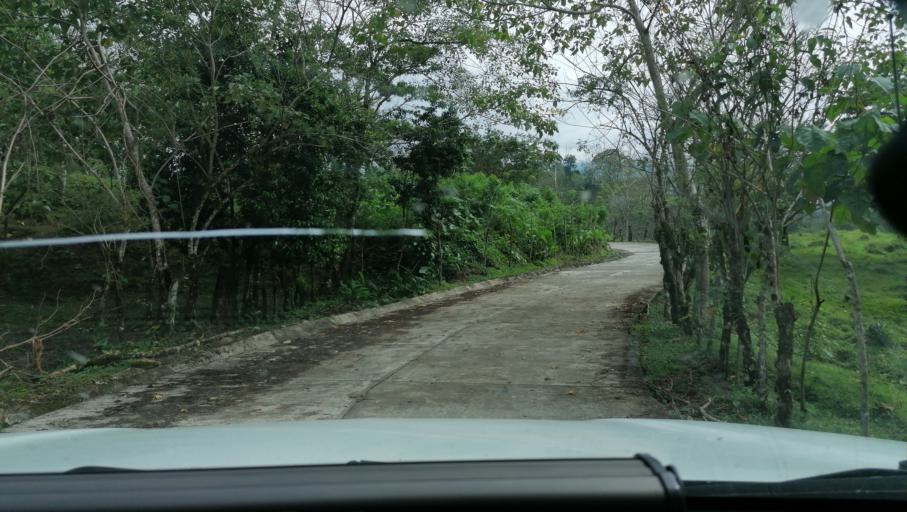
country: MX
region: Chiapas
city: Ocotepec
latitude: 17.3257
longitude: -93.1675
